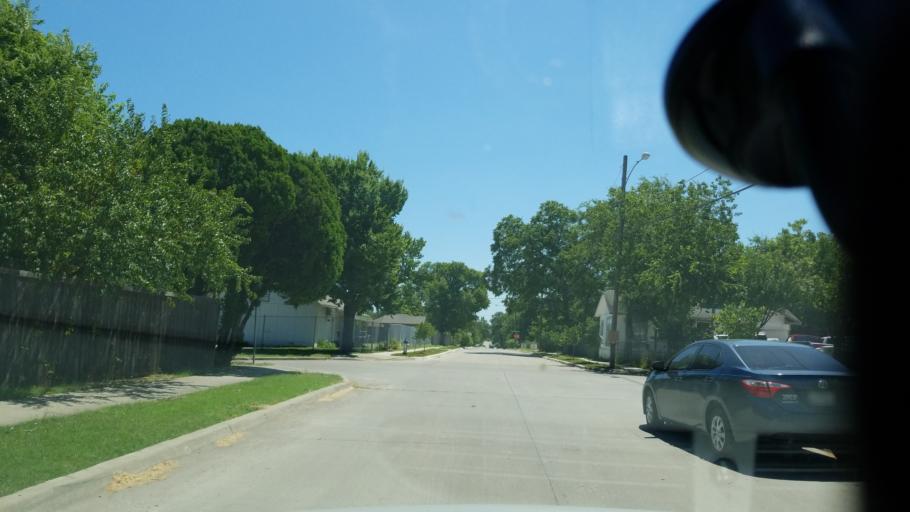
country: US
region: Texas
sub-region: Dallas County
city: Cockrell Hill
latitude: 32.7096
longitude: -96.8221
